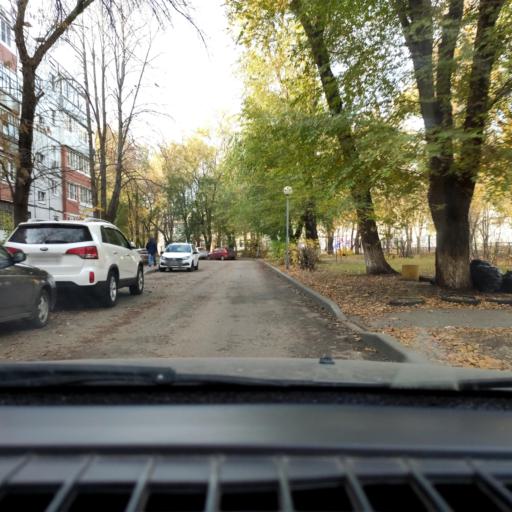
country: RU
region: Samara
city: Tol'yatti
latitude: 53.5130
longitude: 49.2705
